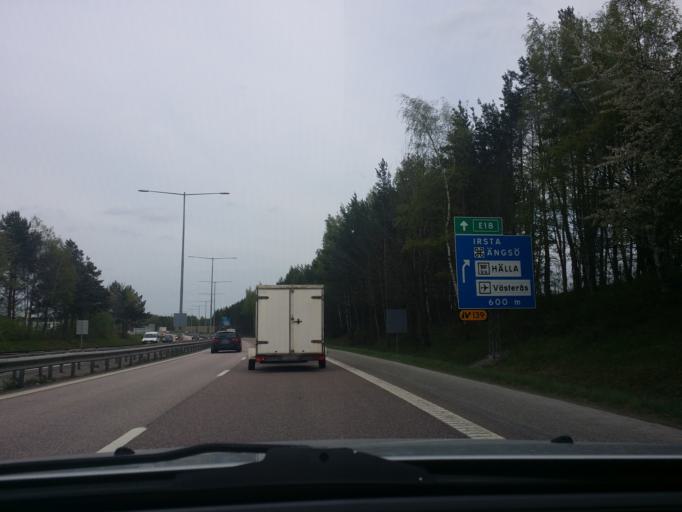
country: SE
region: Vaestmanland
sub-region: Vasteras
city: Vasteras
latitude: 59.6068
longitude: 16.6111
